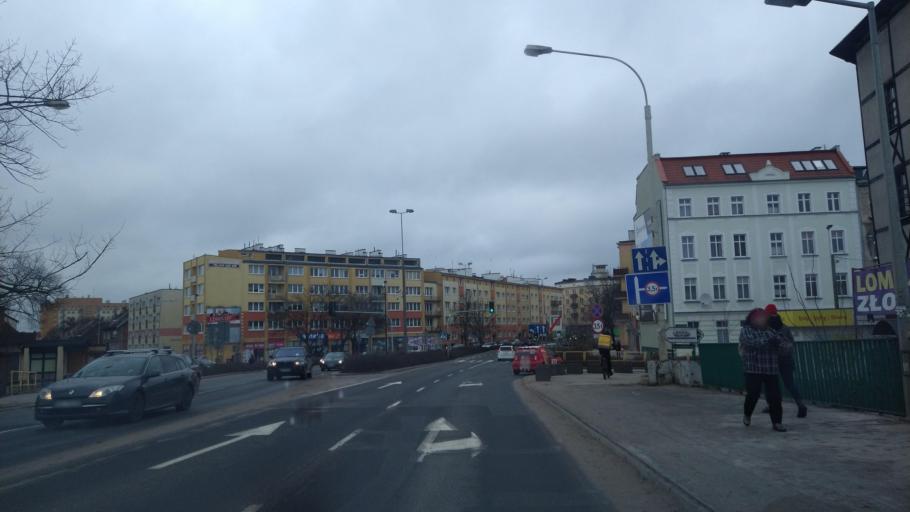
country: PL
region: Warmian-Masurian Voivodeship
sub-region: Powiat olsztynski
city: Olsztyn
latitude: 53.7846
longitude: 20.4920
